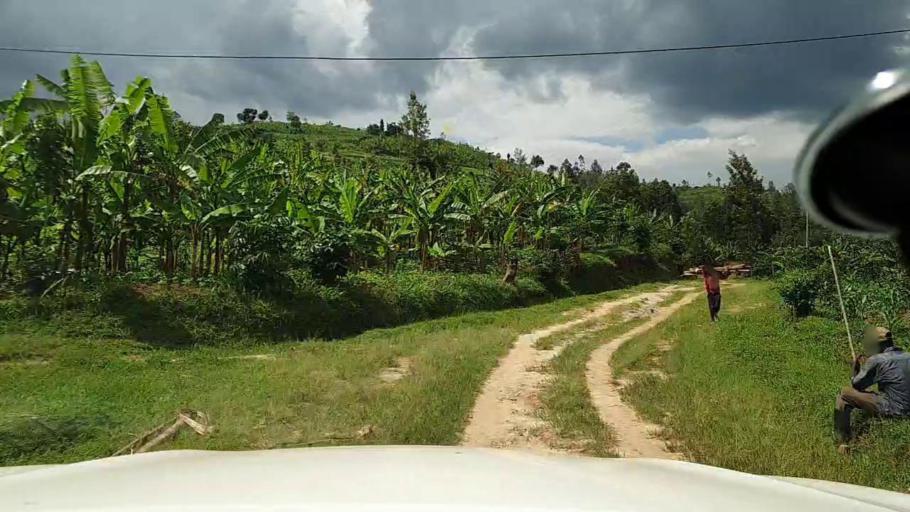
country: RW
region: Southern Province
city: Gitarama
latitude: -1.8260
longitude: 29.8021
